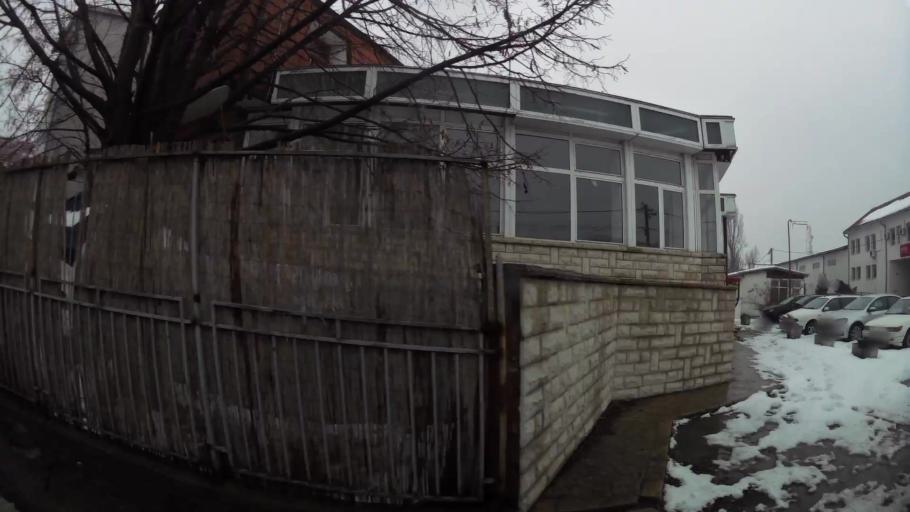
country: RS
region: Central Serbia
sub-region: Belgrade
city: Zemun
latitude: 44.8489
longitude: 20.3589
